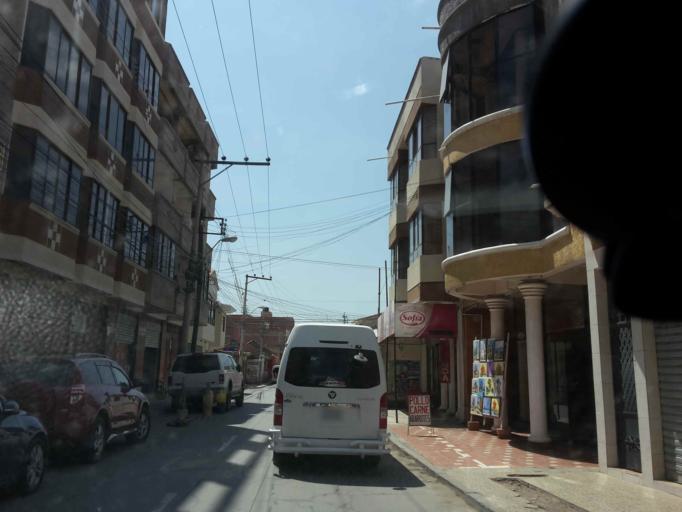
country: BO
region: Cochabamba
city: Cochabamba
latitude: -17.3397
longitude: -66.2183
